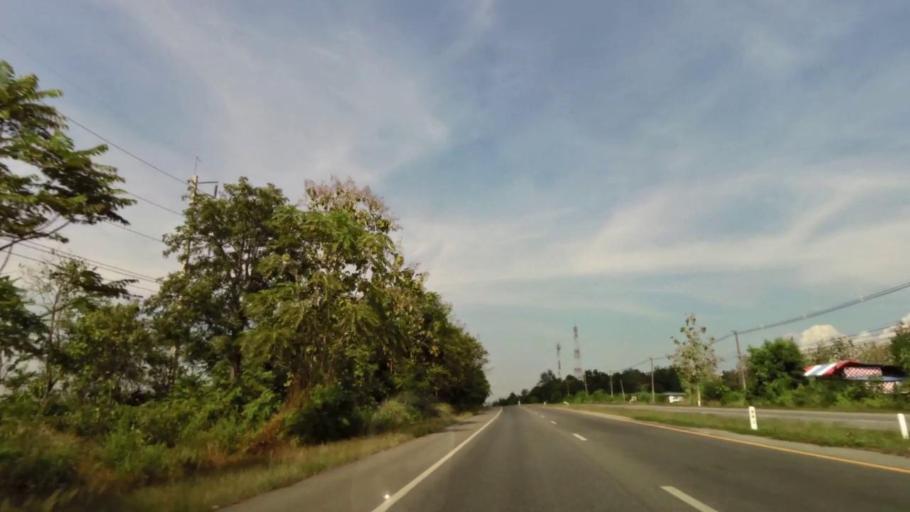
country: TH
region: Uttaradit
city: Tron
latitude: 17.5302
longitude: 100.2113
